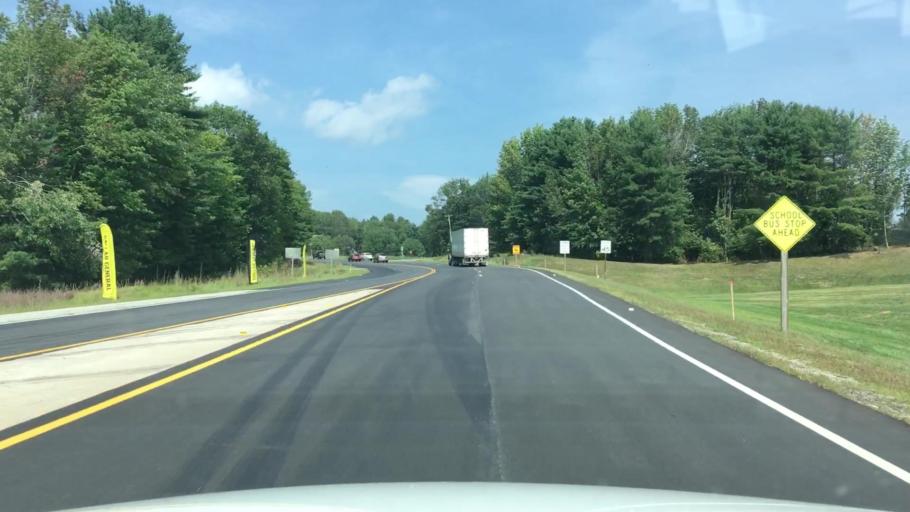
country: US
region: Maine
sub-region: Androscoggin County
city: Turner
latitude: 44.2579
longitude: -70.2589
